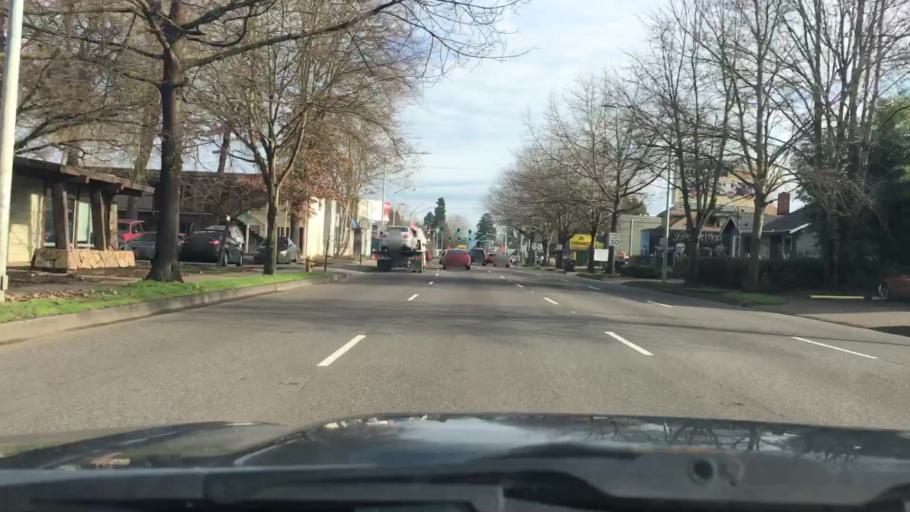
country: US
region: Oregon
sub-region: Lane County
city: Eugene
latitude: 44.0522
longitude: -123.1082
